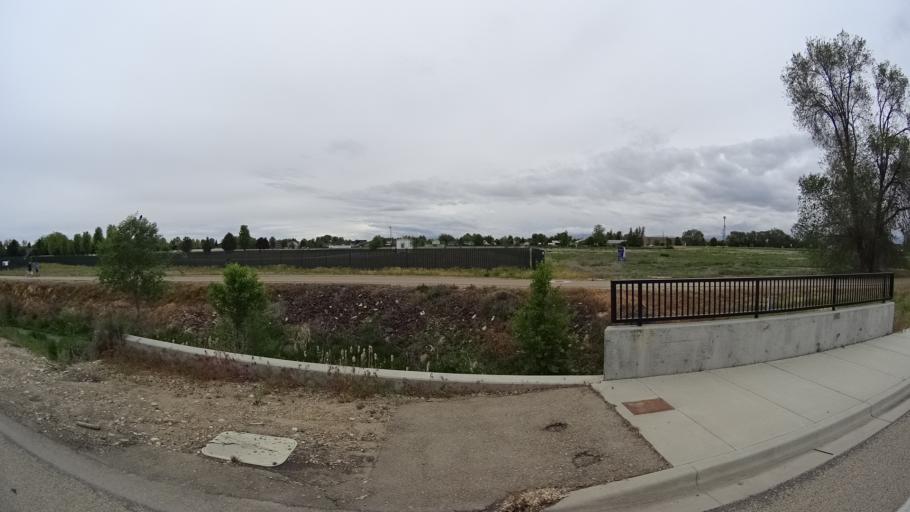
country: US
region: Idaho
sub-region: Ada County
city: Meridian
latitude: 43.6336
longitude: -116.4158
